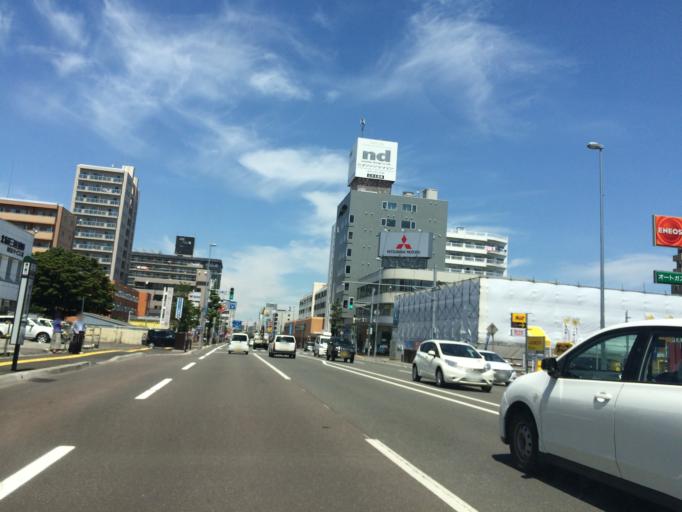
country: JP
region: Hokkaido
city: Sapporo
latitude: 43.0458
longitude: 141.3429
